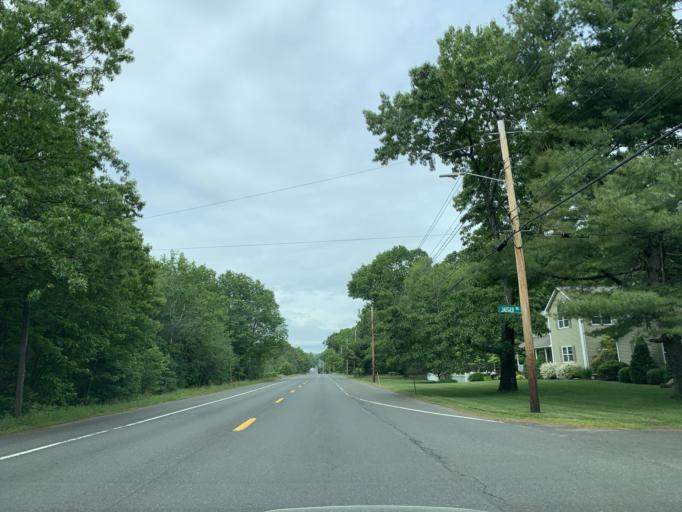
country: US
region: Massachusetts
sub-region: Hampshire County
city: Southampton
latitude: 42.1813
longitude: -72.7175
